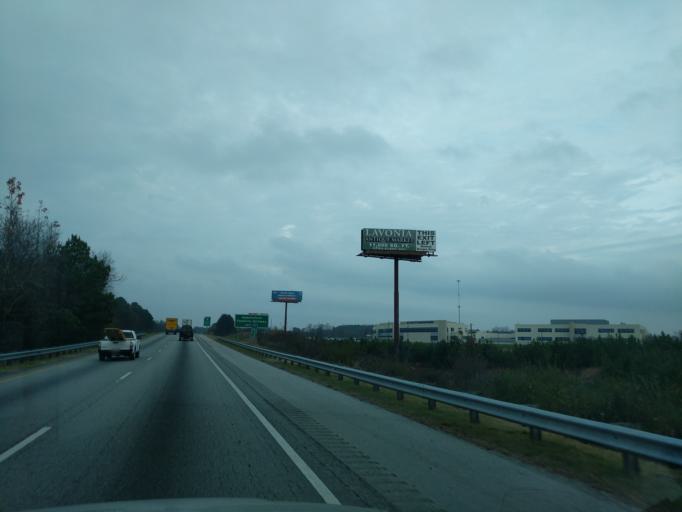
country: US
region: Georgia
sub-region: Franklin County
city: Lavonia
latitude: 34.4374
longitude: -83.1408
